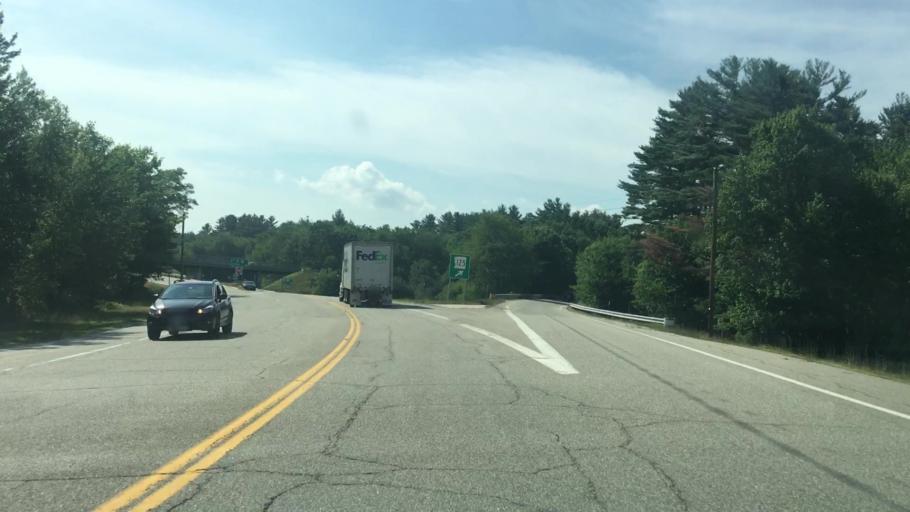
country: US
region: New Hampshire
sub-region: Strafford County
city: Rochester
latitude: 43.3303
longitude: -70.9704
